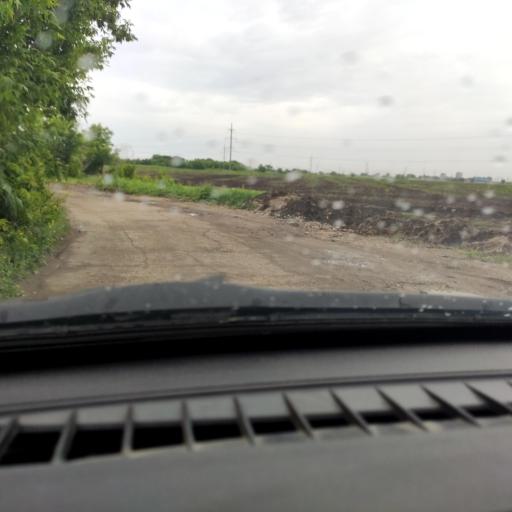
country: RU
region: Samara
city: Tol'yatti
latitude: 53.5895
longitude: 49.4360
